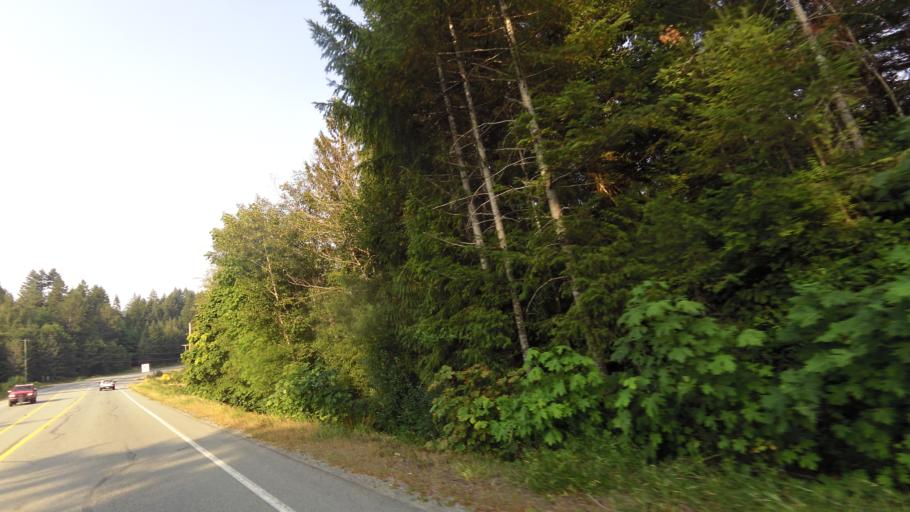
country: CA
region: British Columbia
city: Port Alberni
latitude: 49.2845
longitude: -124.9786
